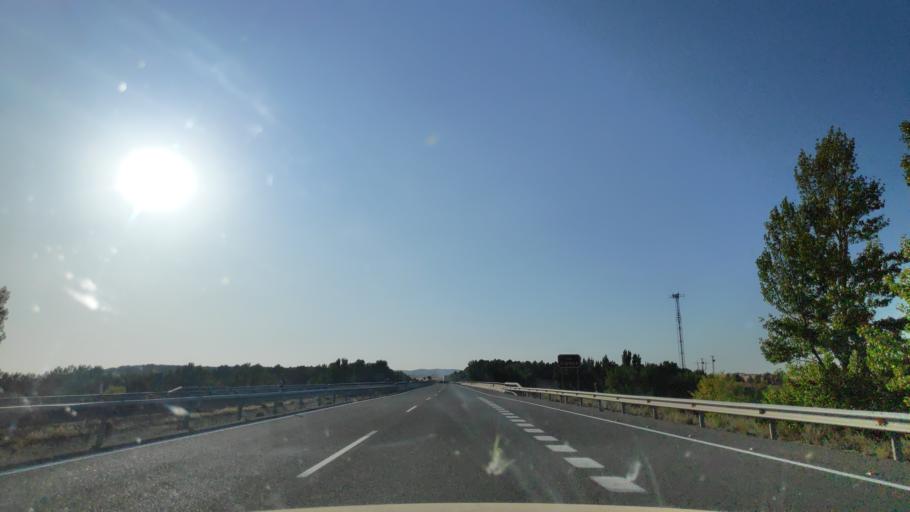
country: ES
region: Castille-La Mancha
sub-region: Provincia de Cuenca
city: Montalbo
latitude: 39.9051
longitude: -2.7188
